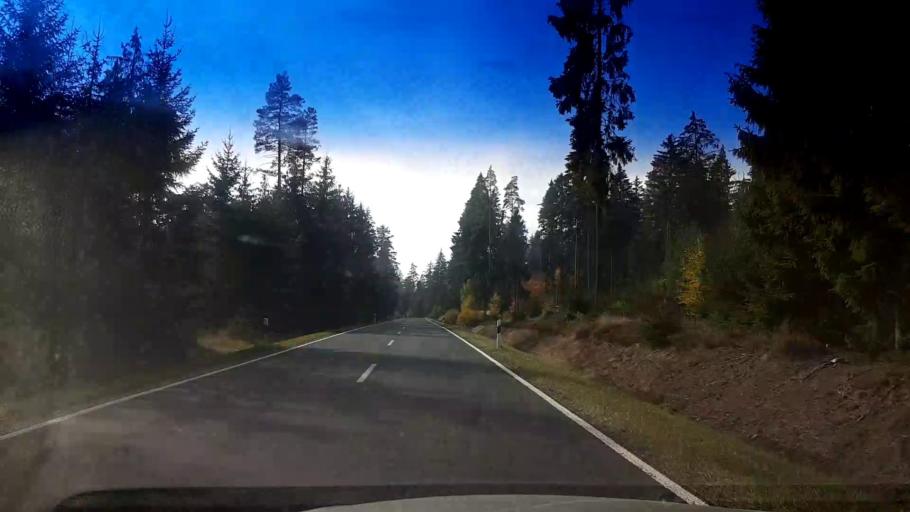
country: DE
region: Bavaria
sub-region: Upper Franconia
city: Schirnding
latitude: 50.0598
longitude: 12.2463
